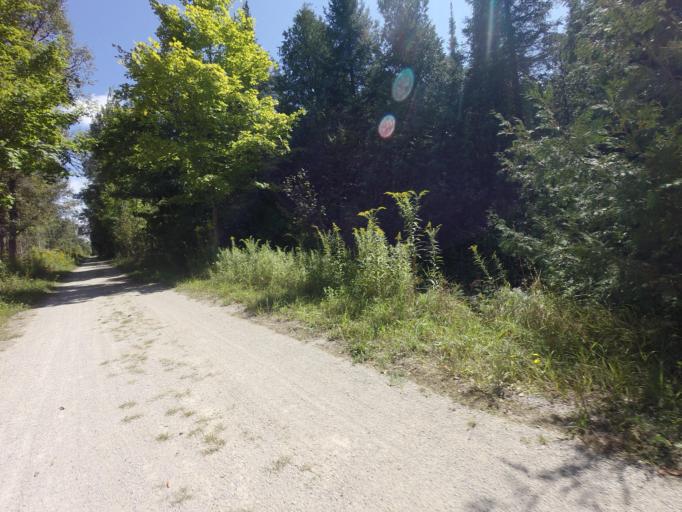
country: CA
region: Ontario
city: Orangeville
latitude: 43.7758
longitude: -80.1068
